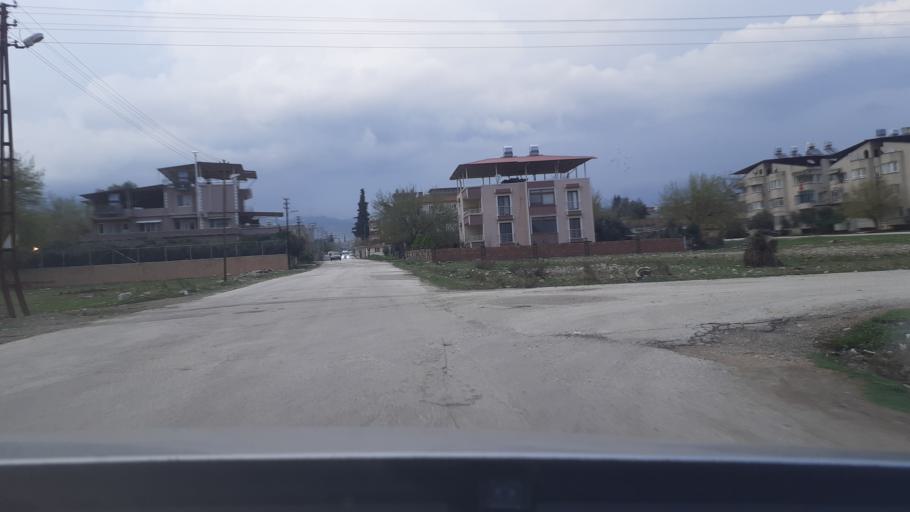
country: TR
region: Hatay
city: Kirikhan
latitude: 36.4852
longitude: 36.3556
